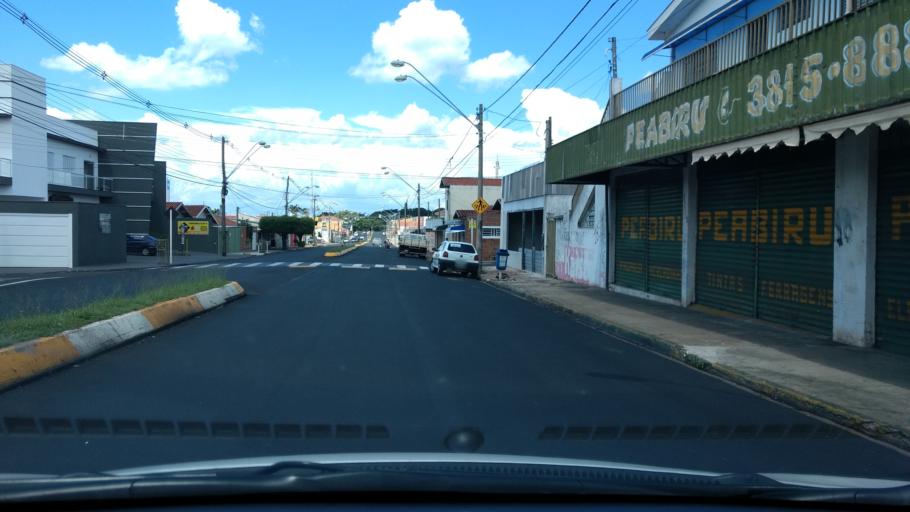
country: BR
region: Sao Paulo
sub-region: Botucatu
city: Botucatu
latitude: -22.8654
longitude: -48.4503
